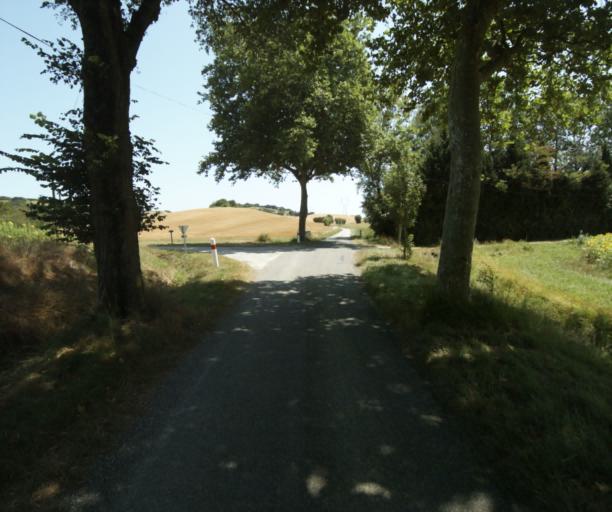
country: FR
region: Midi-Pyrenees
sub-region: Departement de la Haute-Garonne
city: Saint-Felix-Lauragais
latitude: 43.4439
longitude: 1.8559
